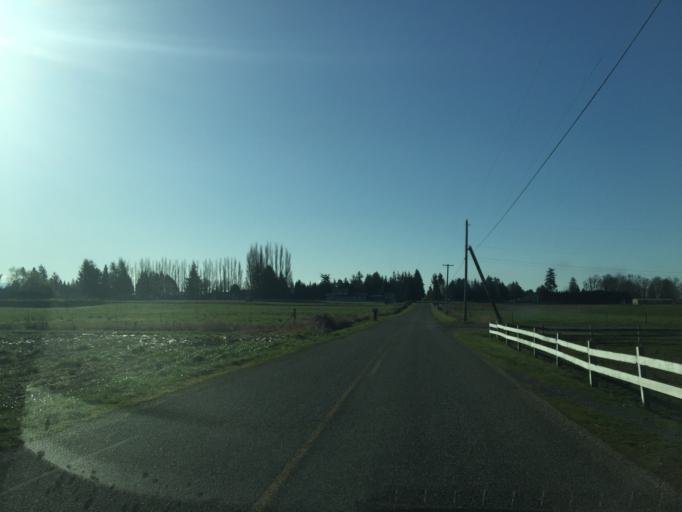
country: US
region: Washington
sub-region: Whatcom County
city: Lynden
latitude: 48.9140
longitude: -122.4642
